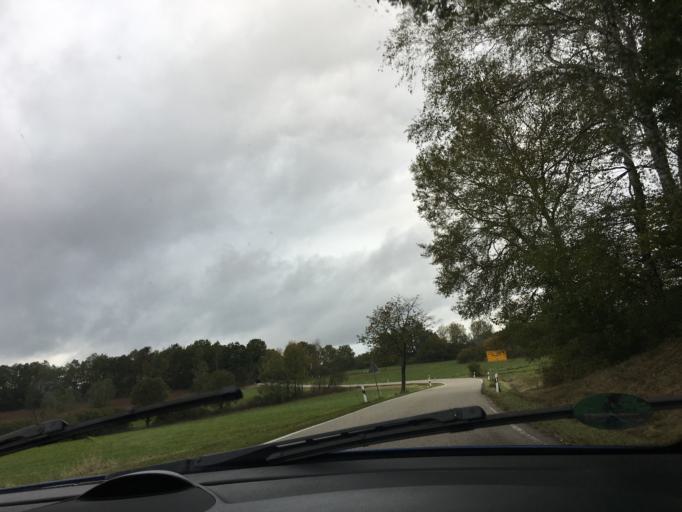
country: DE
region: Rheinland-Pfalz
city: Schmalenberg
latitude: 49.3263
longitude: 7.7493
